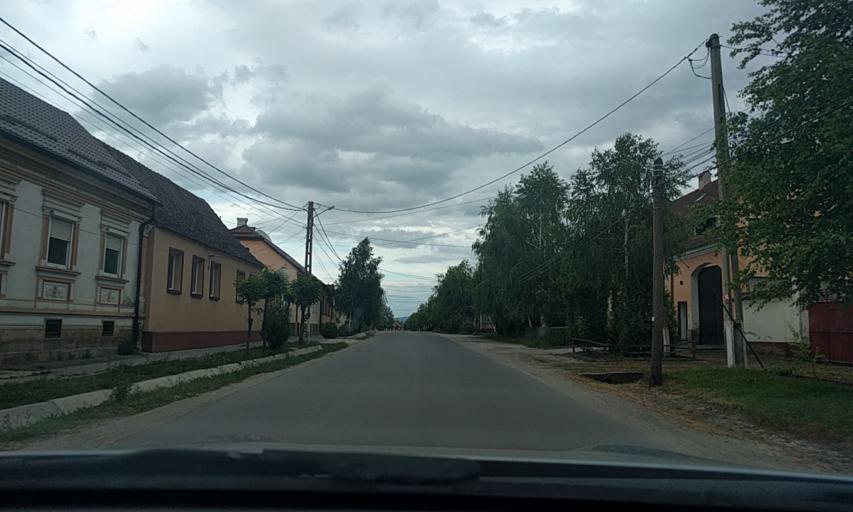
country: RO
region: Brasov
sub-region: Comuna Harman
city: Harman
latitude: 45.7141
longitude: 25.6873
